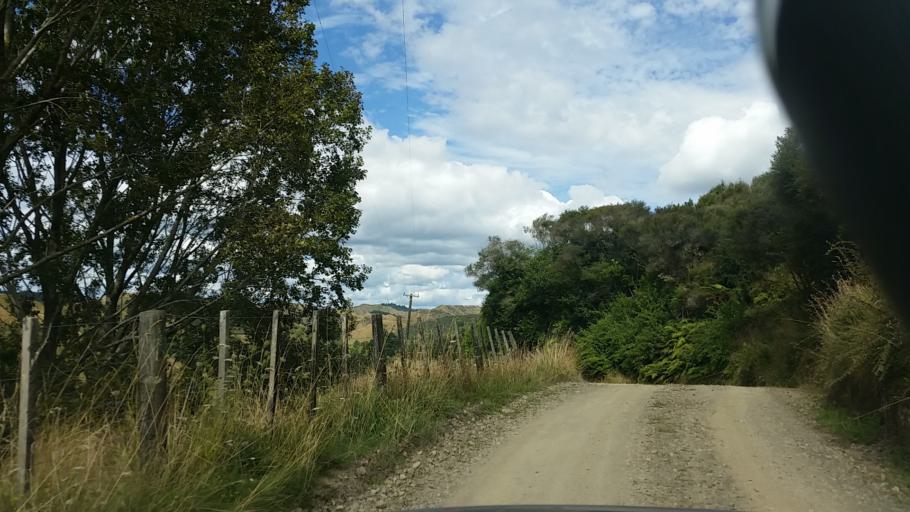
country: NZ
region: Taranaki
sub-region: South Taranaki District
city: Eltham
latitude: -39.2503
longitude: 174.5650
